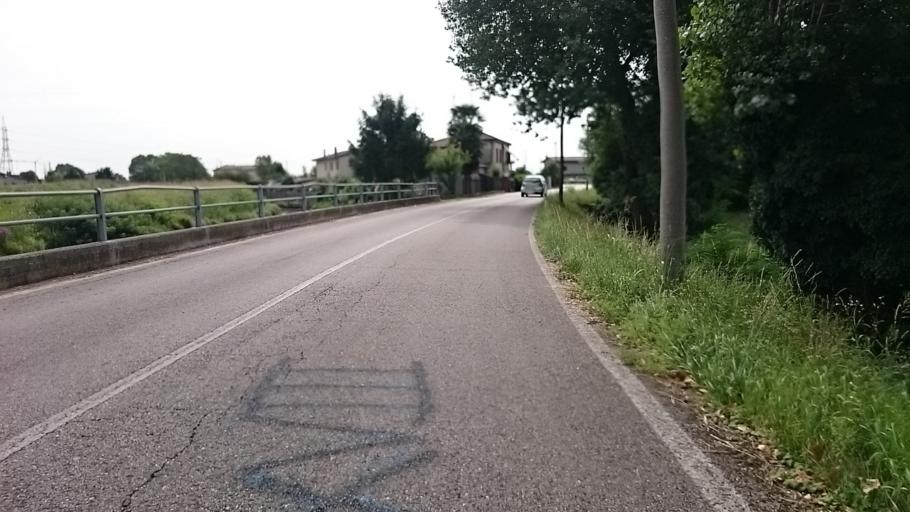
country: IT
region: Veneto
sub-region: Provincia di Venezia
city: Fornase
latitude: 45.4566
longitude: 12.1977
